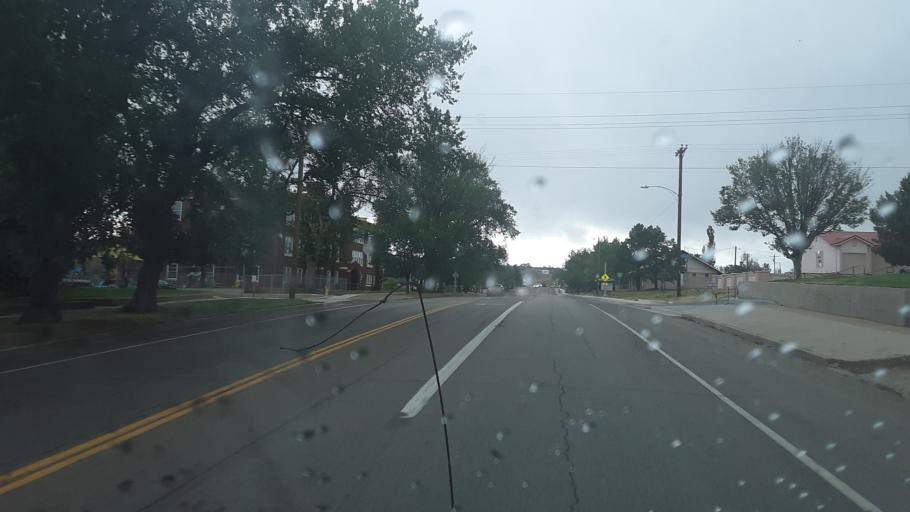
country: US
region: Colorado
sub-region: Huerfano County
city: Walsenburg
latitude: 37.6303
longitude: -104.7855
